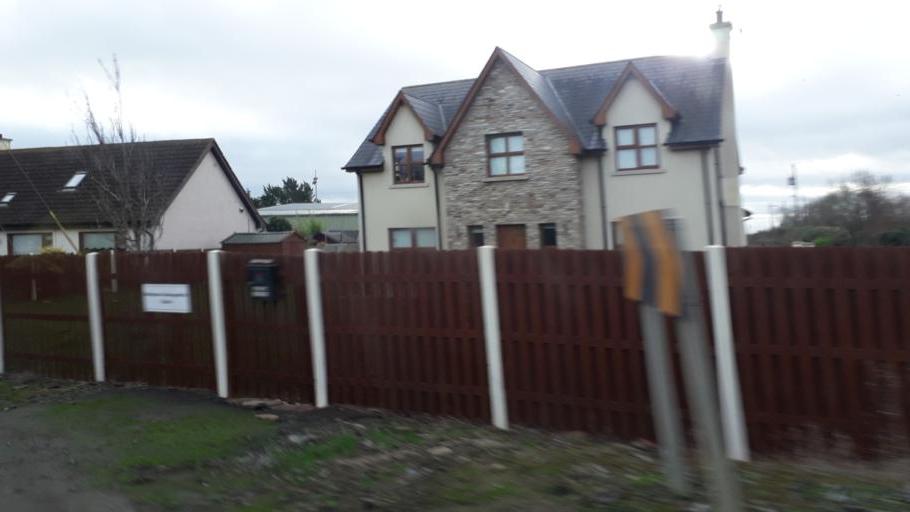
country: IE
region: Leinster
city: An Ros
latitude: 53.5474
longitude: -6.1142
